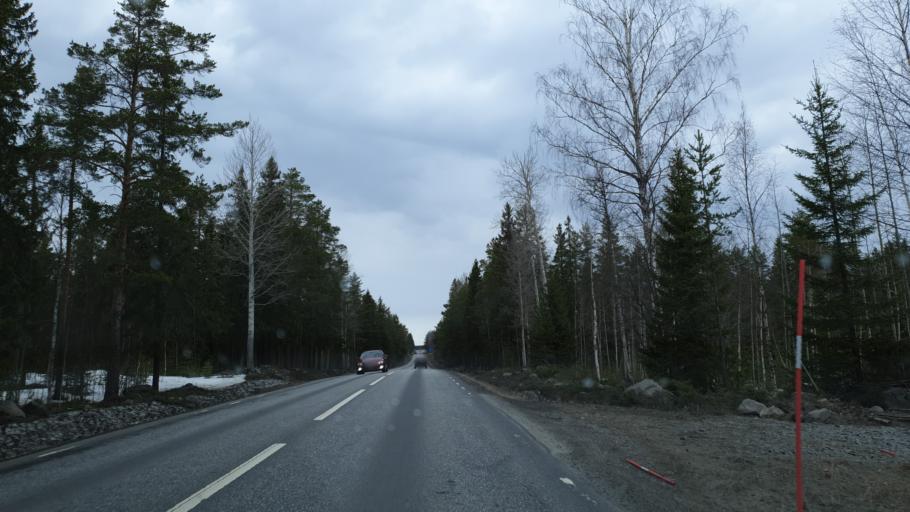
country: SE
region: Vaesterbotten
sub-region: Skelleftea Kommun
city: Viken
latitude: 64.6562
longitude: 20.9538
